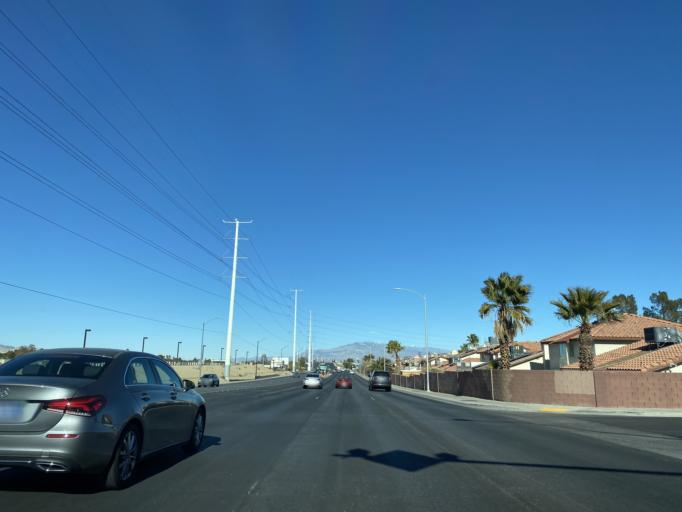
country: US
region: Nevada
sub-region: Clark County
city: Spring Valley
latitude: 36.1706
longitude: -115.2779
